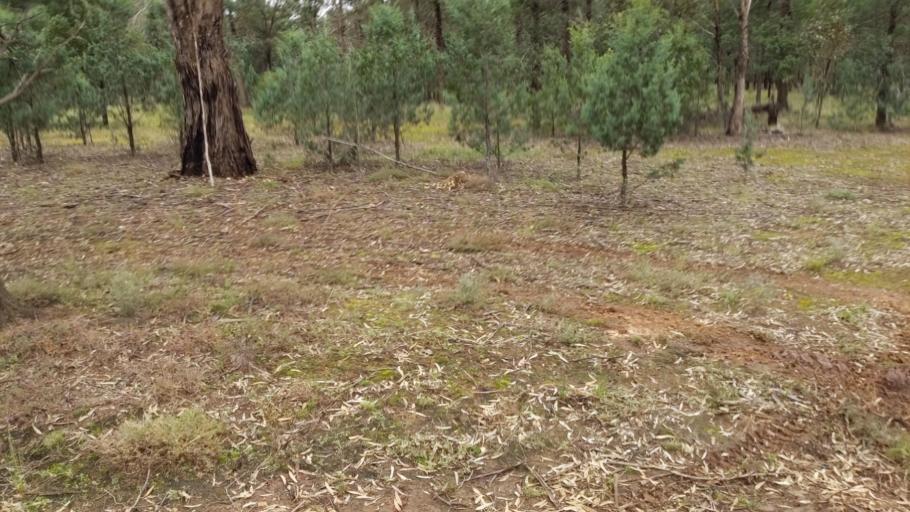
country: AU
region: New South Wales
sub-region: Coolamon
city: Coolamon
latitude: -34.8590
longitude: 146.9260
